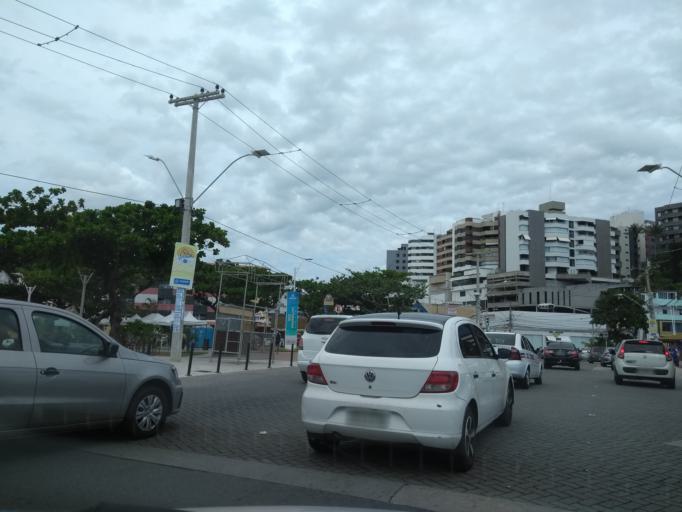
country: BR
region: Bahia
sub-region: Salvador
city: Salvador
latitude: -13.0140
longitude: -38.4888
